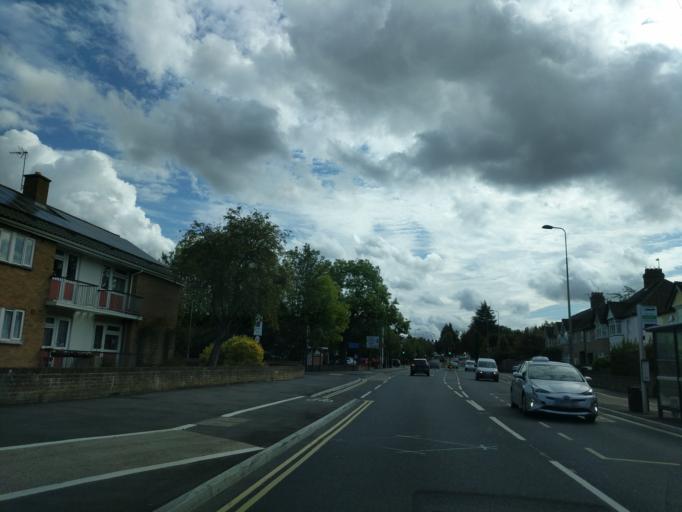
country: GB
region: England
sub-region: Oxfordshire
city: Oxford
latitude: 51.7642
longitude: -1.2261
